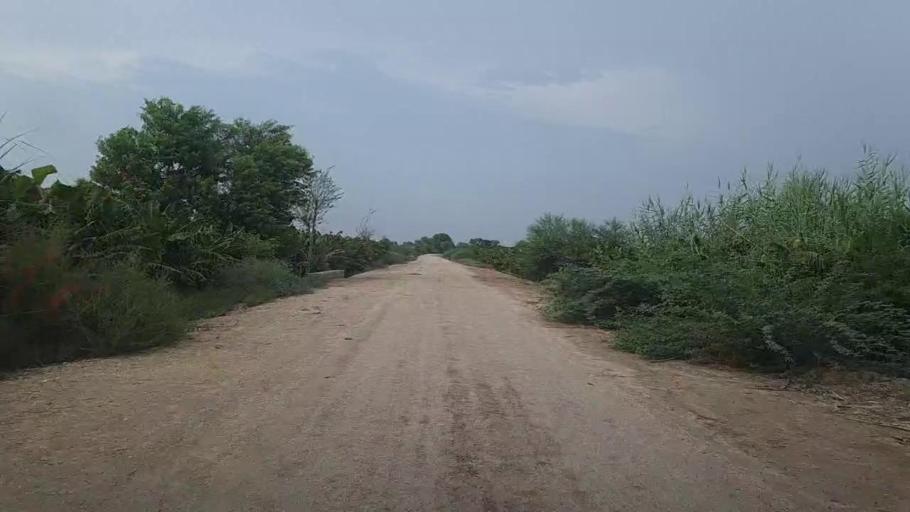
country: PK
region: Sindh
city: Karaundi
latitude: 26.9796
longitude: 68.4339
